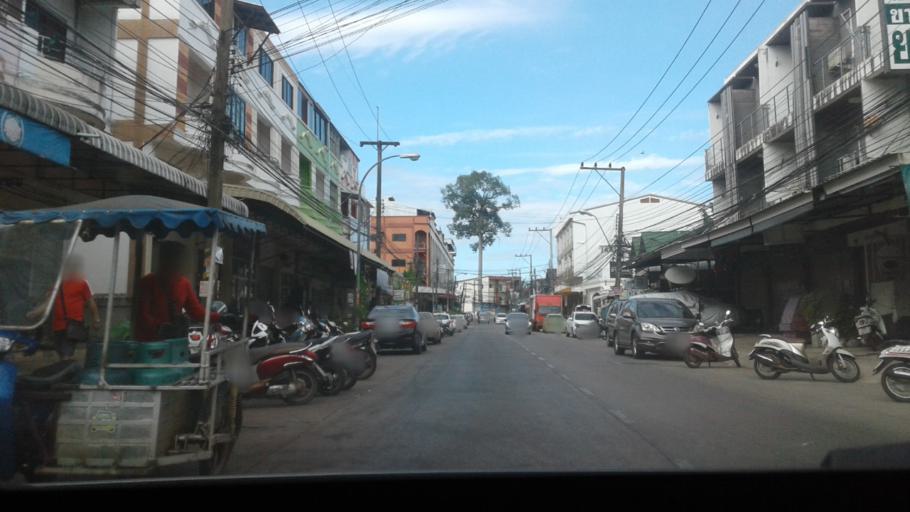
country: TH
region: Changwat Udon Thani
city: Udon Thani
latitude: 17.4156
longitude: 102.8001
